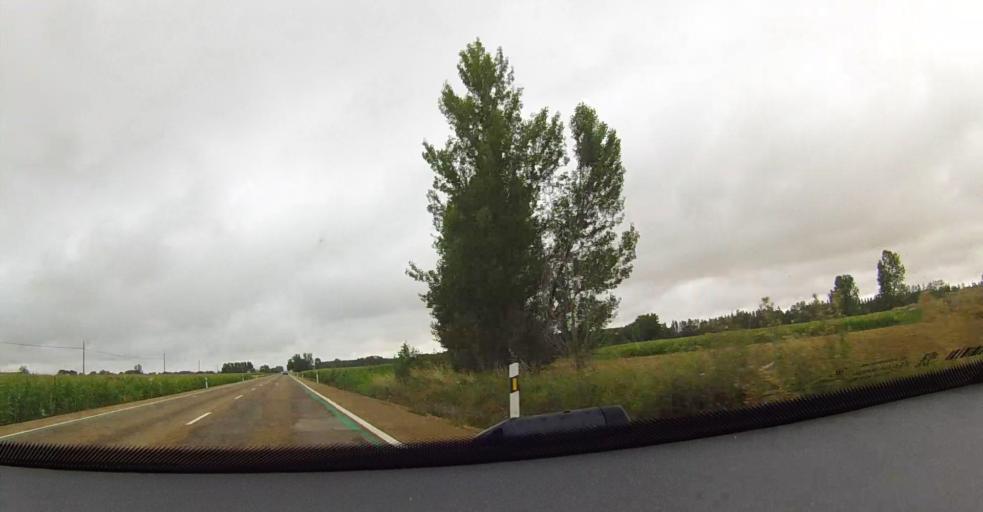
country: ES
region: Castille and Leon
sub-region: Provincia de Palencia
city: Nogal de las Huertas
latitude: 42.3965
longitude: -4.6616
